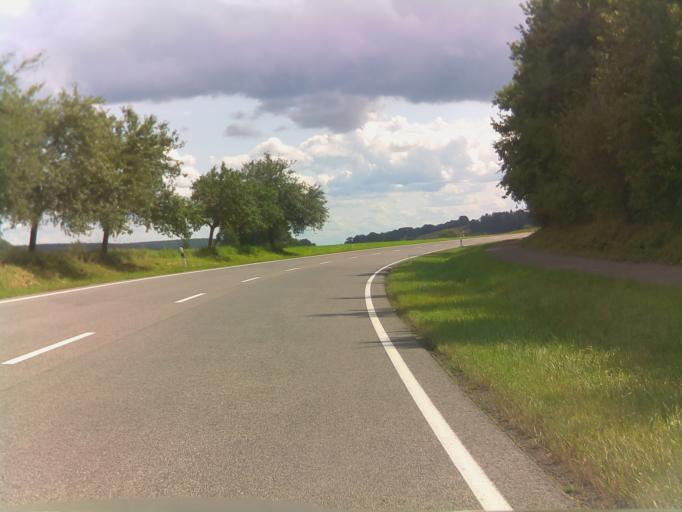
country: DE
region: Bavaria
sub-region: Regierungsbezirk Unterfranken
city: Rentweinsdorf
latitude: 50.0553
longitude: 10.8110
